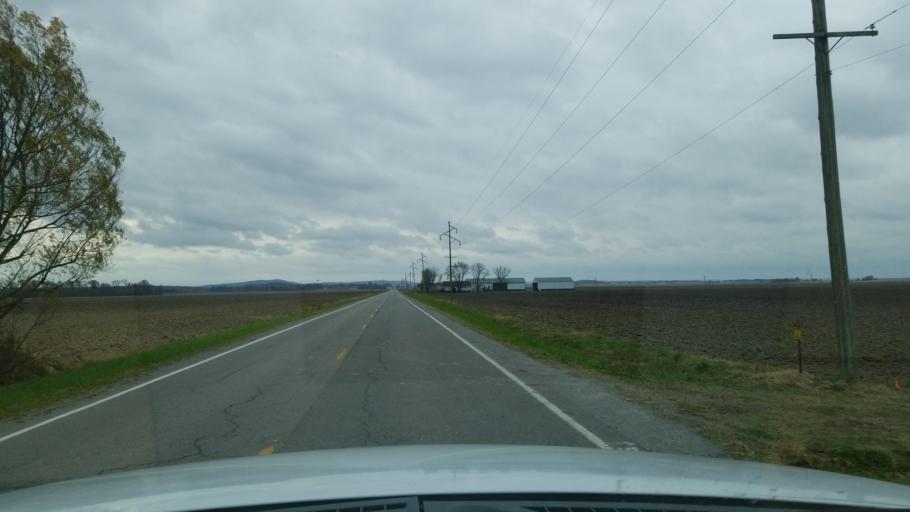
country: US
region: Illinois
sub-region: Saline County
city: Eldorado
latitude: 37.7867
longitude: -88.4382
